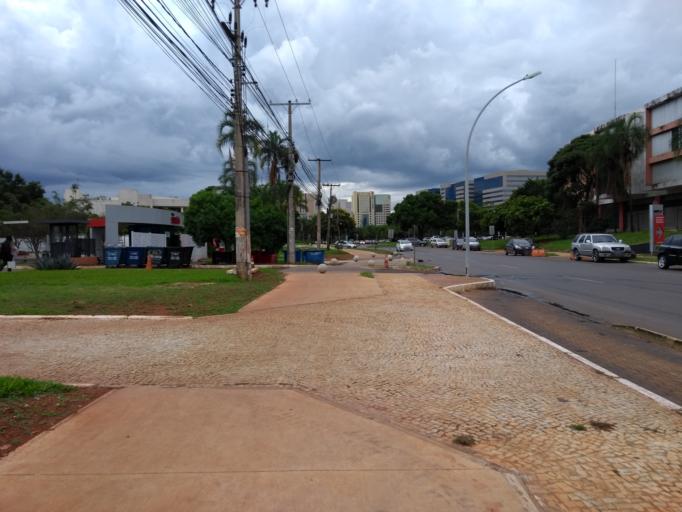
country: BR
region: Federal District
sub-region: Brasilia
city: Brasilia
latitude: -15.7982
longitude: -47.8972
